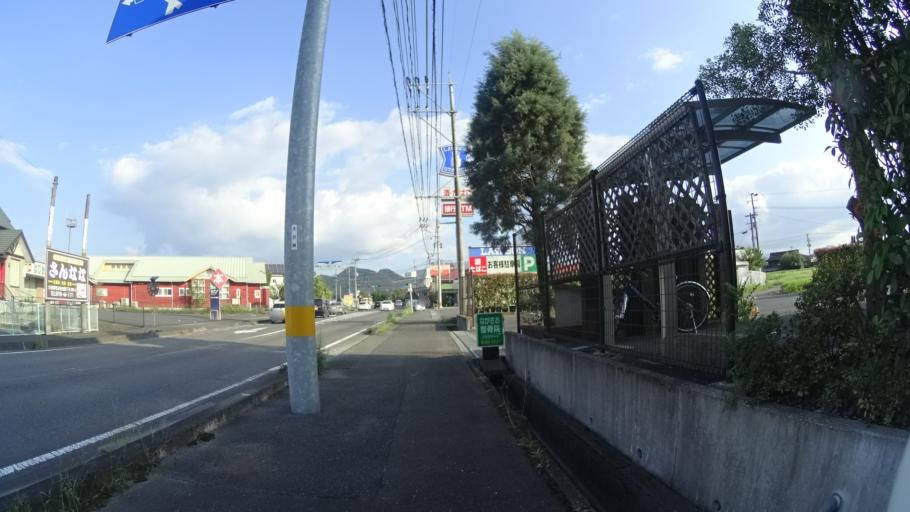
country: JP
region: Oita
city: Bungo-Takada-shi
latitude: 33.4405
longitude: 131.3527
